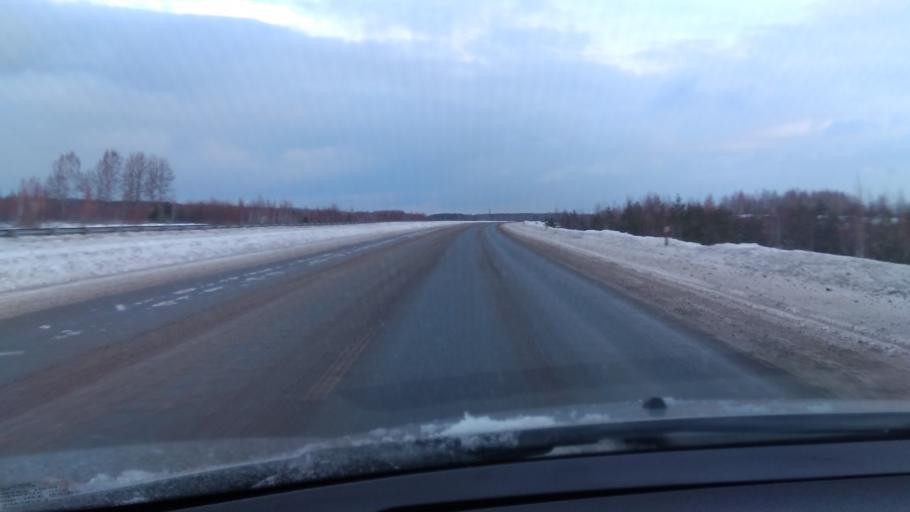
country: RU
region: Sverdlovsk
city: Nev'yansk
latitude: 57.5171
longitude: 60.1803
